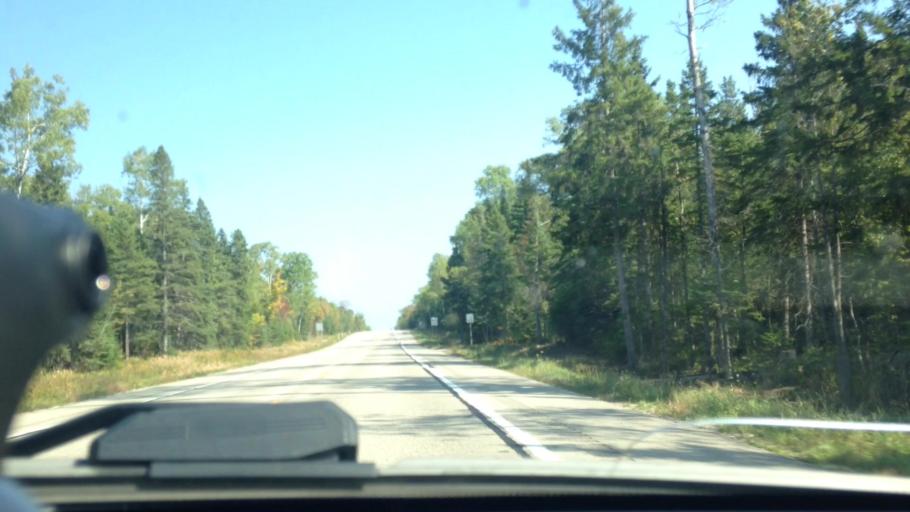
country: US
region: Michigan
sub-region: Luce County
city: Newberry
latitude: 46.3036
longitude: -85.2974
